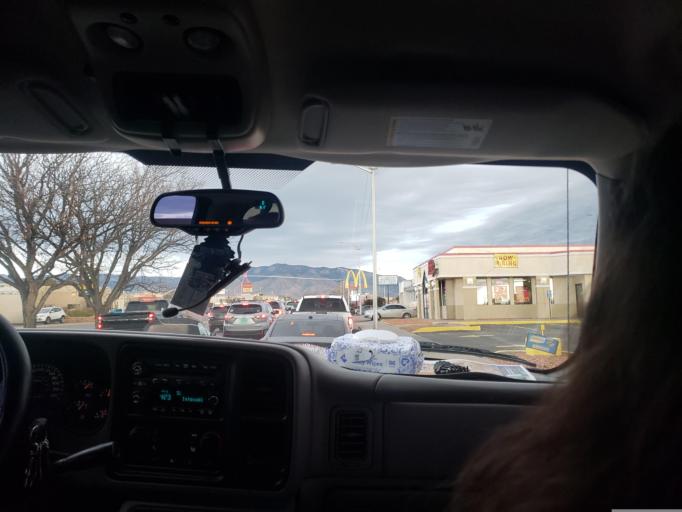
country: US
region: New Mexico
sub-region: Bernalillo County
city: Albuquerque
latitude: 35.1092
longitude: -106.5801
